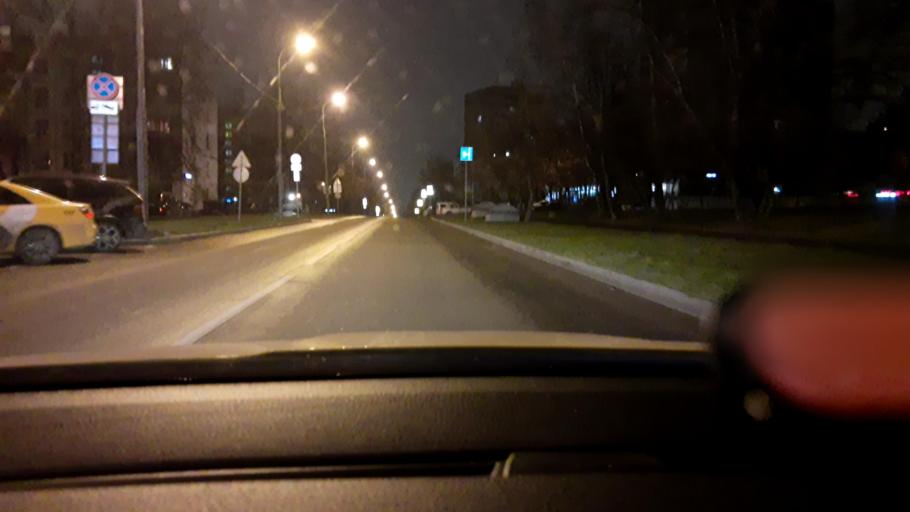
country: RU
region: Moscow
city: Zyuzino
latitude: 55.6632
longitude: 37.5830
